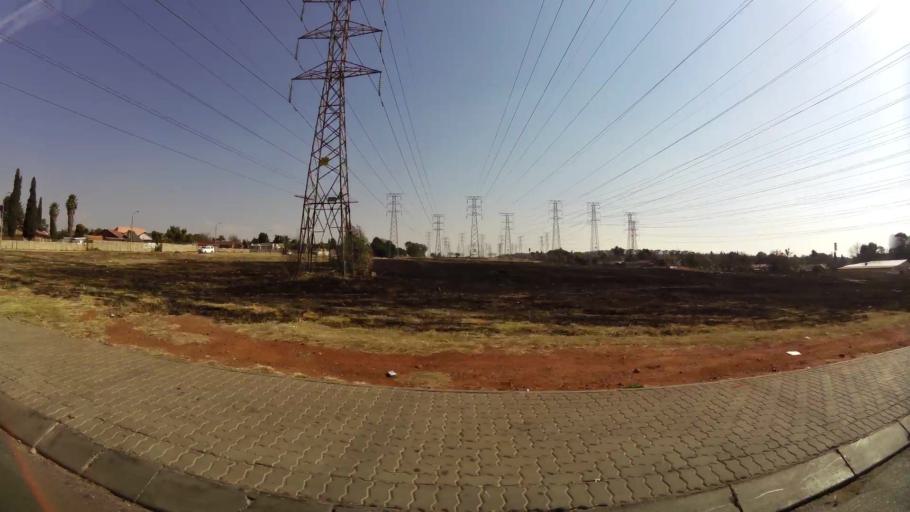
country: ZA
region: Gauteng
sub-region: City of Johannesburg Metropolitan Municipality
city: Modderfontein
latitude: -26.1203
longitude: 28.1710
